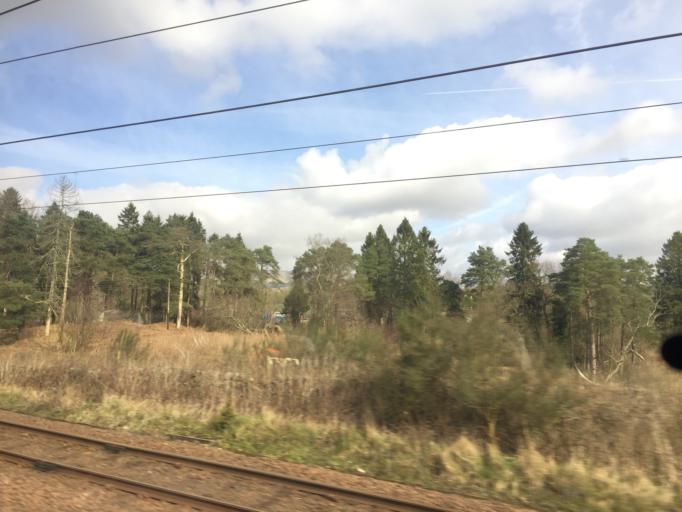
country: GB
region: Scotland
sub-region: Dumfries and Galloway
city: Moffat
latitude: 55.3119
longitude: -3.4595
